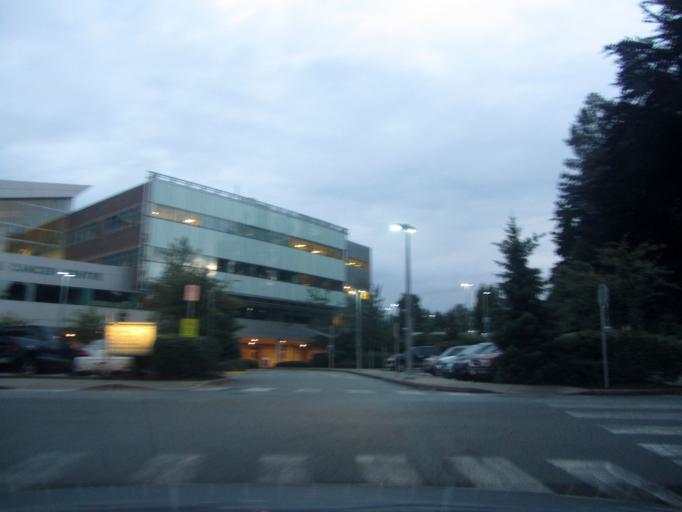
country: US
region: Washington
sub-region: Whatcom County
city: Sumas
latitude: 49.0377
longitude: -122.3113
